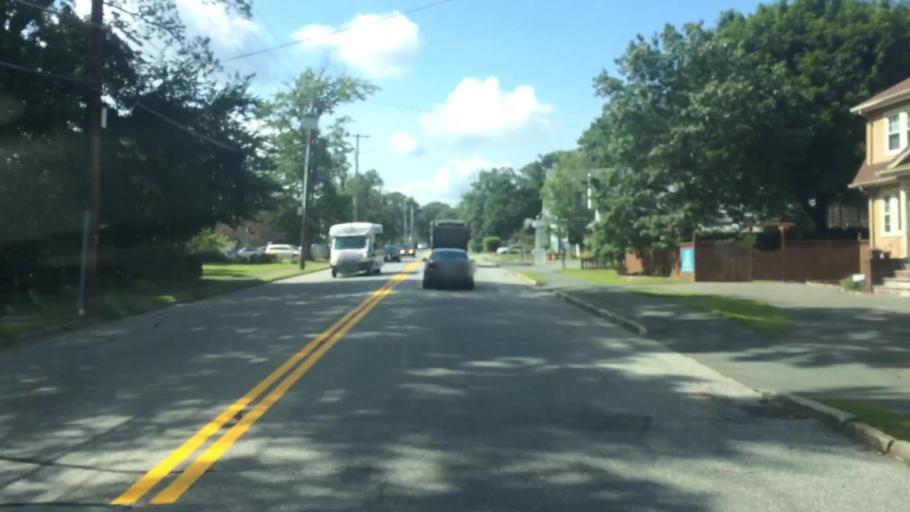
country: US
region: Massachusetts
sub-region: Essex County
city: South Peabody
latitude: 42.5008
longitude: -70.9771
